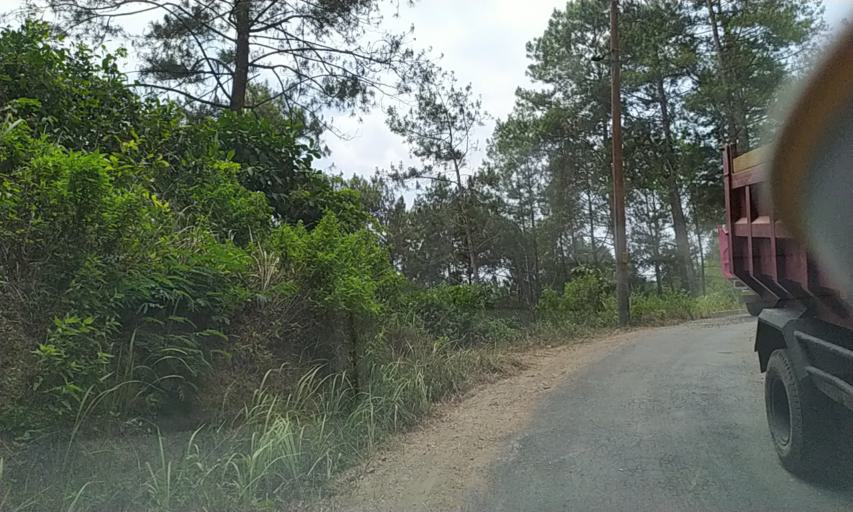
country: ID
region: Central Java
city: Jambuluwuk
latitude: -7.3282
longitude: 108.9326
